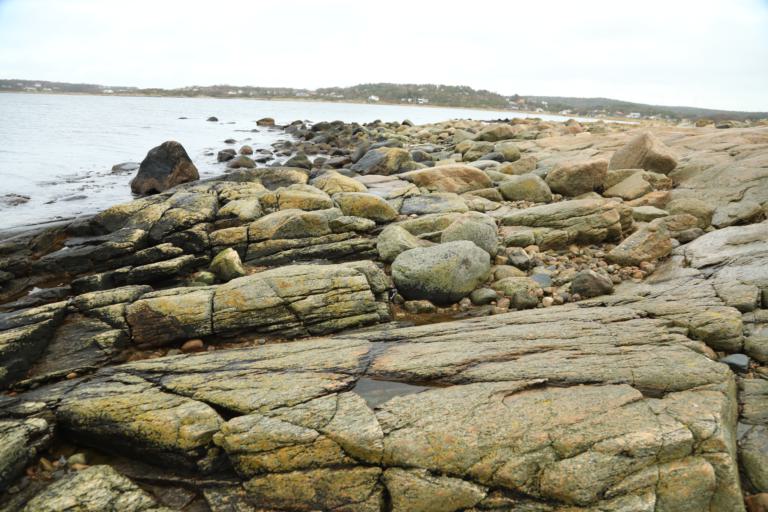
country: SE
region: Halland
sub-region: Varbergs Kommun
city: Varberg
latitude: 57.1798
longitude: 12.2038
